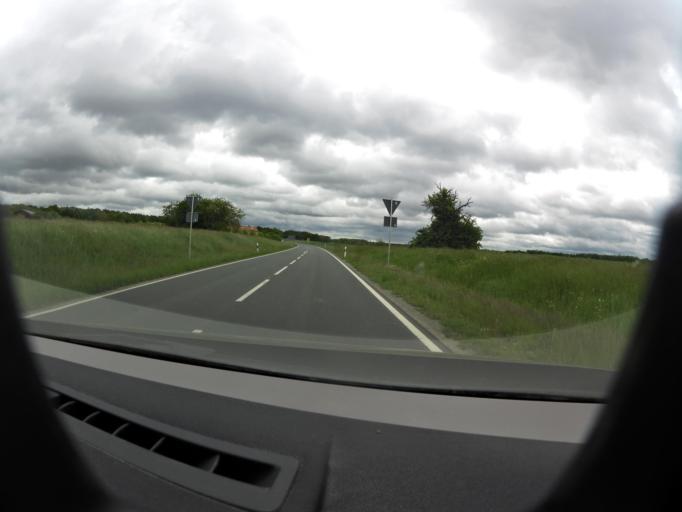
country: DE
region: Bavaria
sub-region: Regierungsbezirk Unterfranken
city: Volkach
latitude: 49.8593
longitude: 10.2434
